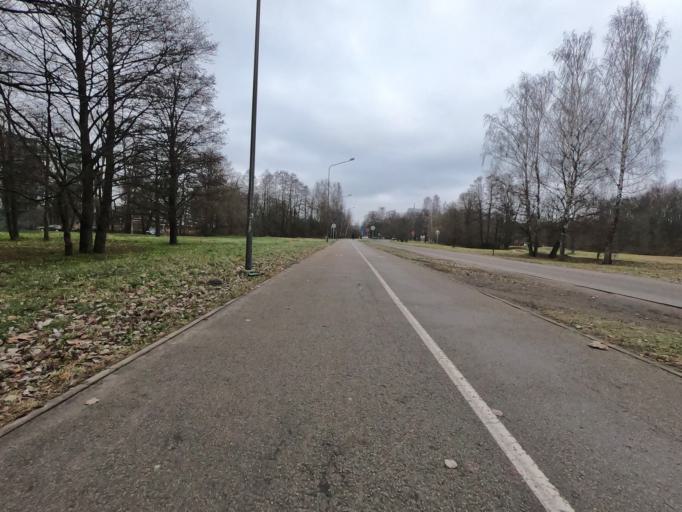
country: LV
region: Marupe
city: Marupe
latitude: 56.9515
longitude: 24.0091
